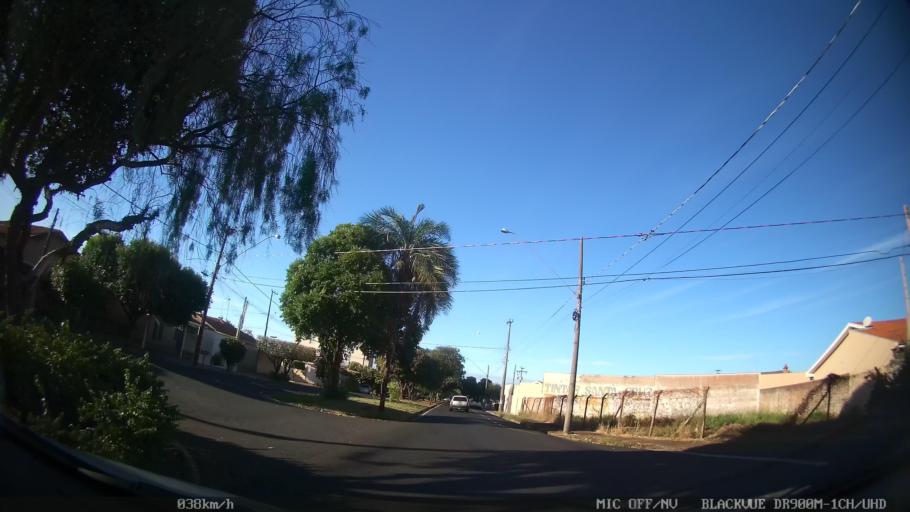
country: BR
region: Sao Paulo
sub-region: Sao Jose Do Rio Preto
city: Sao Jose do Rio Preto
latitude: -20.8316
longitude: -49.3702
